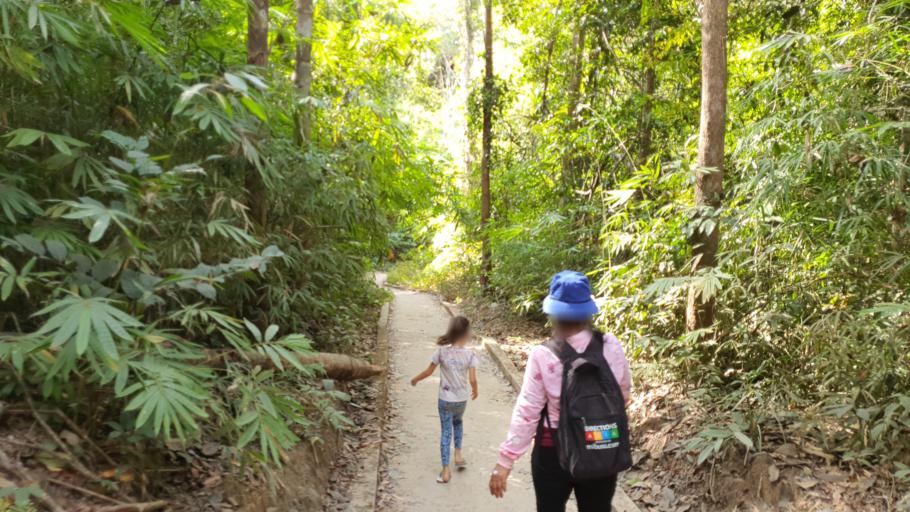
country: TH
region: Nakhon Phanom
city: Ban Phaeng
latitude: 17.9850
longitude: 104.1334
